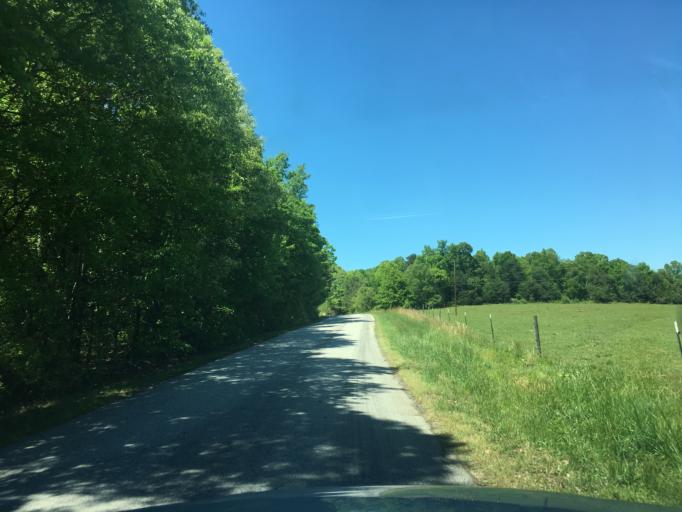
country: US
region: South Carolina
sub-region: Spartanburg County
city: Duncan
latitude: 34.8809
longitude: -82.1813
